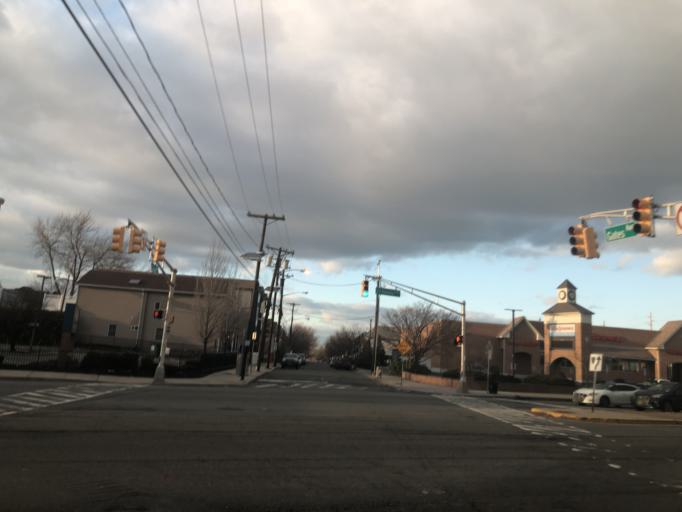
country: US
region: New Jersey
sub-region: Hudson County
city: Bayonne
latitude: 40.6936
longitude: -74.0983
